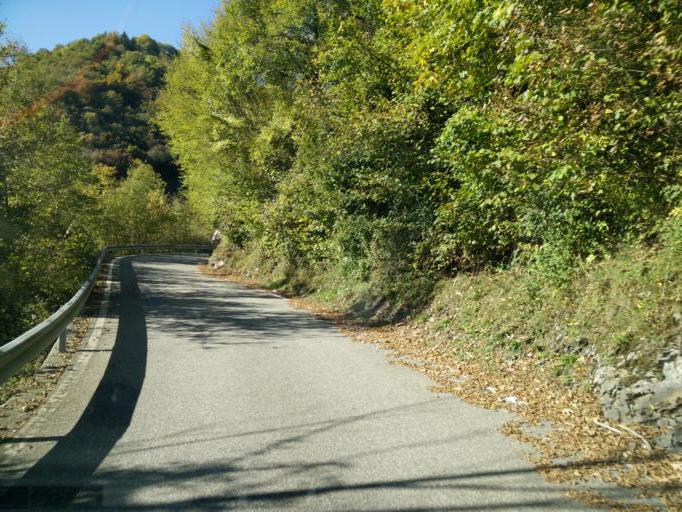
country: IT
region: Lombardy
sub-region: Provincia di Brescia
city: Capovalle
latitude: 45.7513
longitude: 10.5615
